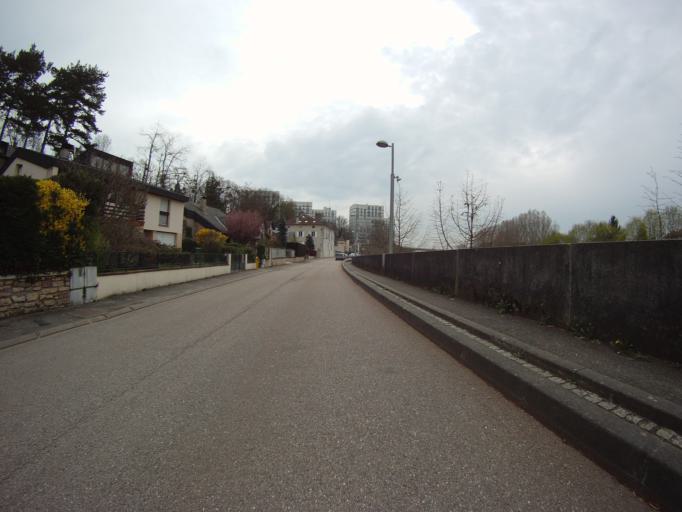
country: FR
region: Lorraine
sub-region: Departement de Meurthe-et-Moselle
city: Malzeville
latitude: 48.7055
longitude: 6.1879
